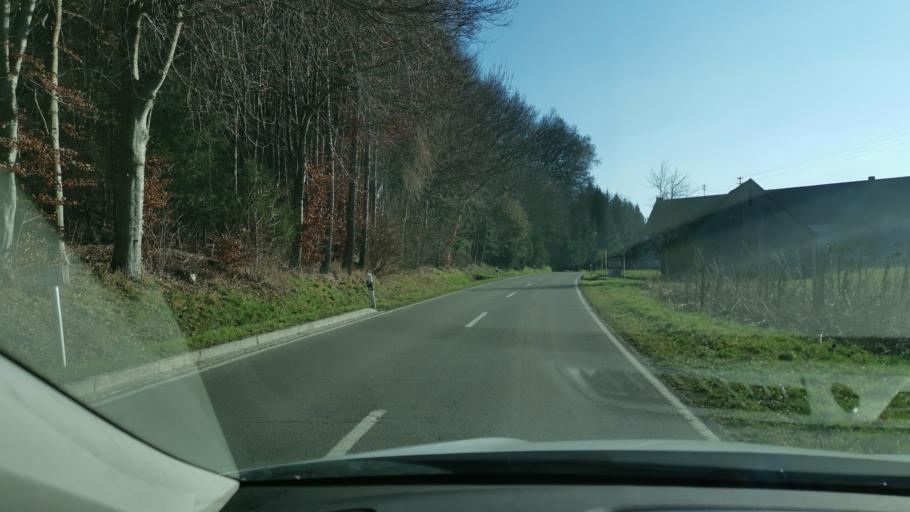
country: DE
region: Bavaria
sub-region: Swabia
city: Rehling
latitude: 48.4916
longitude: 10.9462
